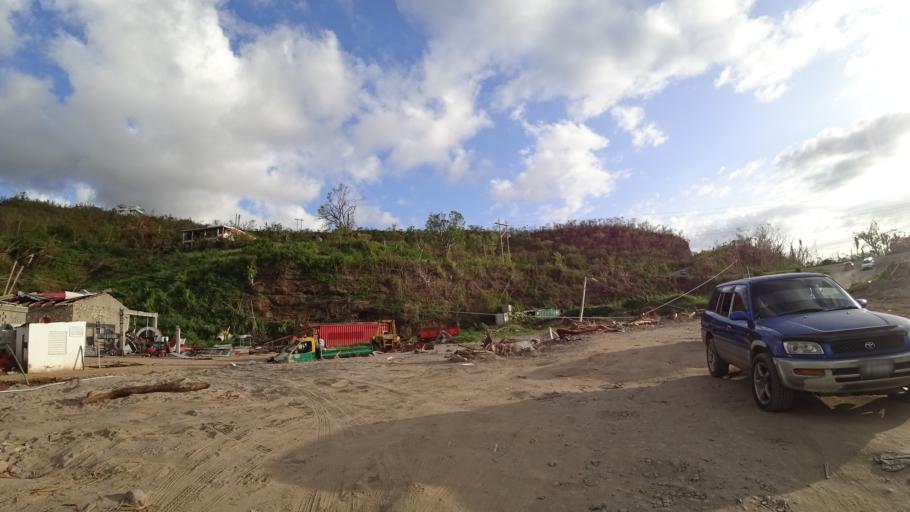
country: DM
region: Saint Joseph
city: Salisbury
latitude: 15.4279
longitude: -61.4329
